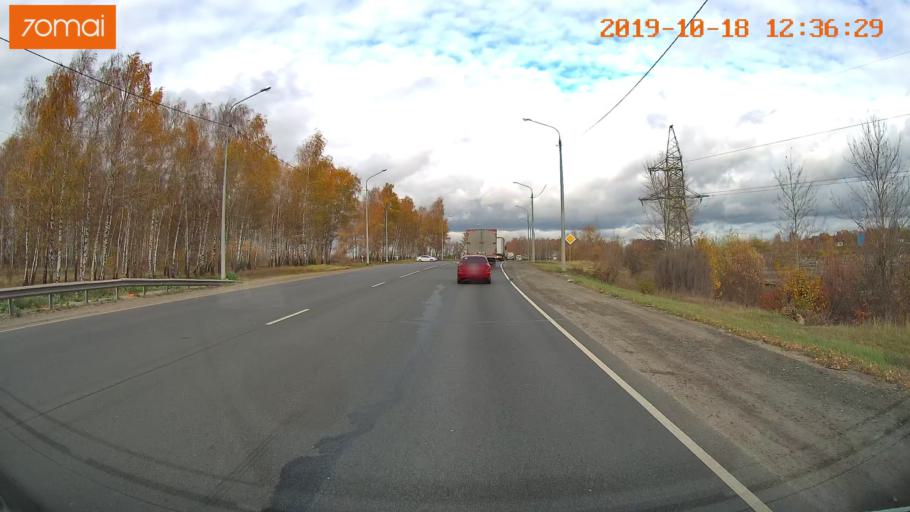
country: RU
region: Rjazan
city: Ryazan'
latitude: 54.6355
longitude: 39.6338
